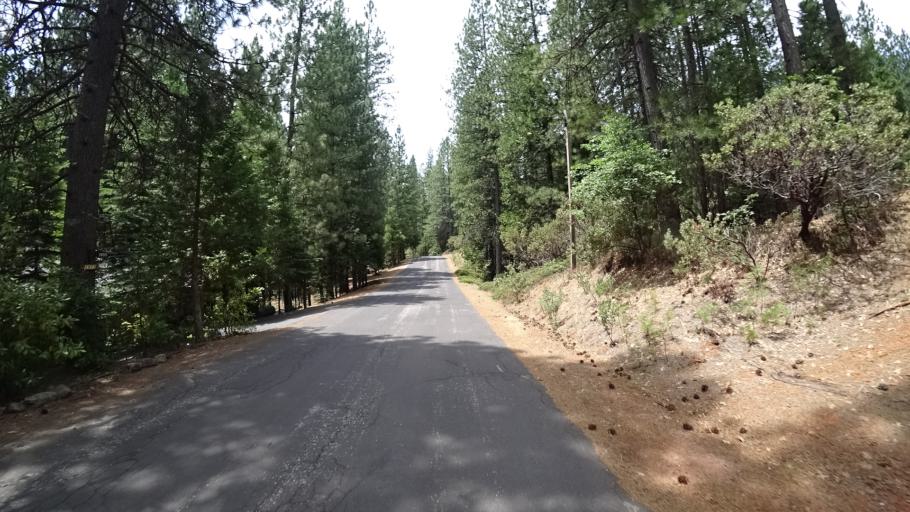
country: US
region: California
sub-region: Calaveras County
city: Arnold
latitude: 38.2382
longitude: -120.3517
